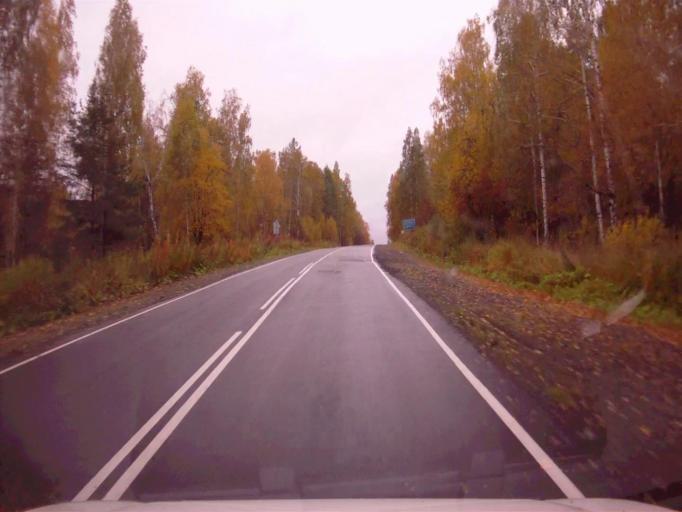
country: RU
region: Chelyabinsk
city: Nizhniy Ufaley
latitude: 56.0559
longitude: 59.9598
